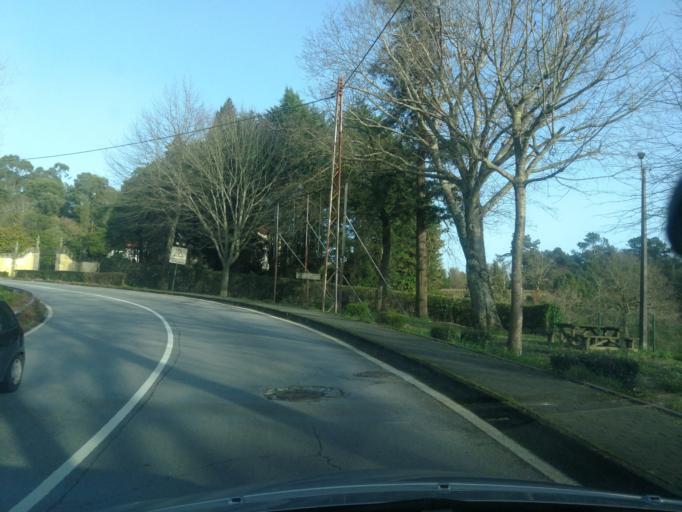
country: PT
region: Braga
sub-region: Barcelos
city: Barcelos
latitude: 41.5245
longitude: -8.6163
